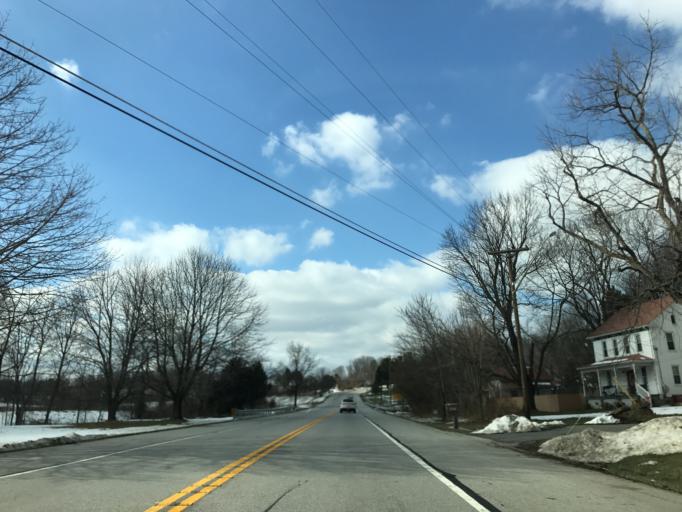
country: US
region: Maryland
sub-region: Carroll County
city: Manchester
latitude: 39.7070
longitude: -76.9150
